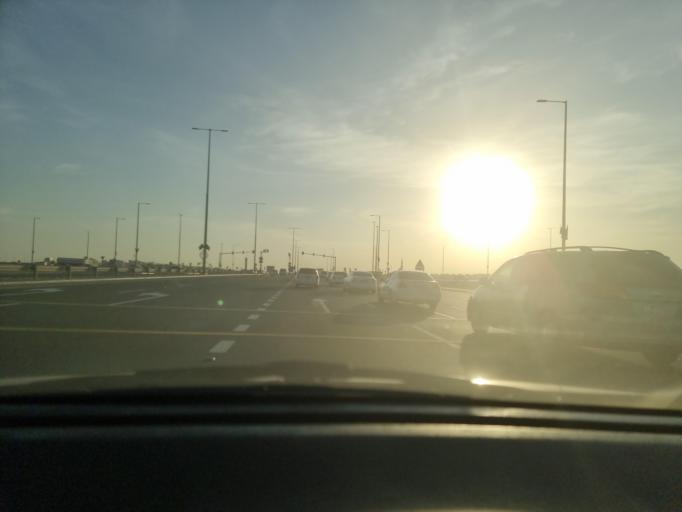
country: AE
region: Abu Dhabi
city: Abu Dhabi
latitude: 24.3387
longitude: 54.7004
